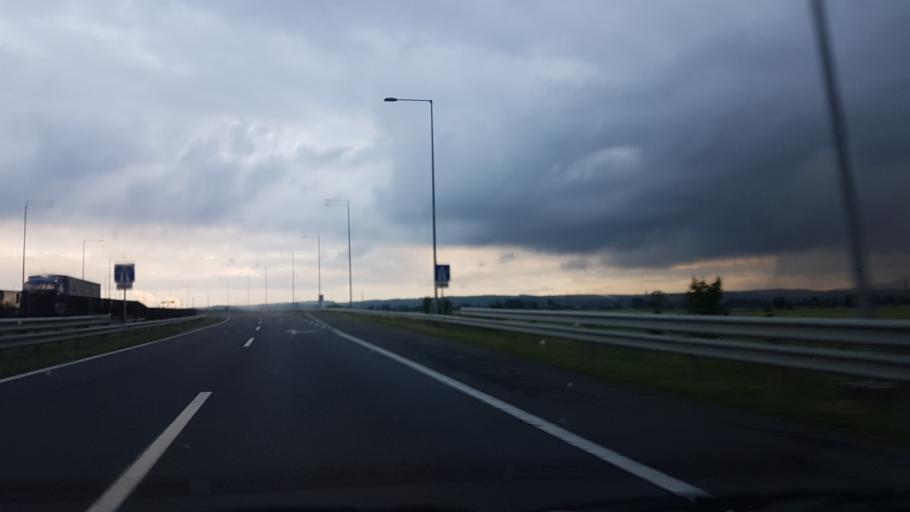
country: HU
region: Borsod-Abauj-Zemplen
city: Alsozsolca
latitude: 48.0654
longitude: 20.8460
